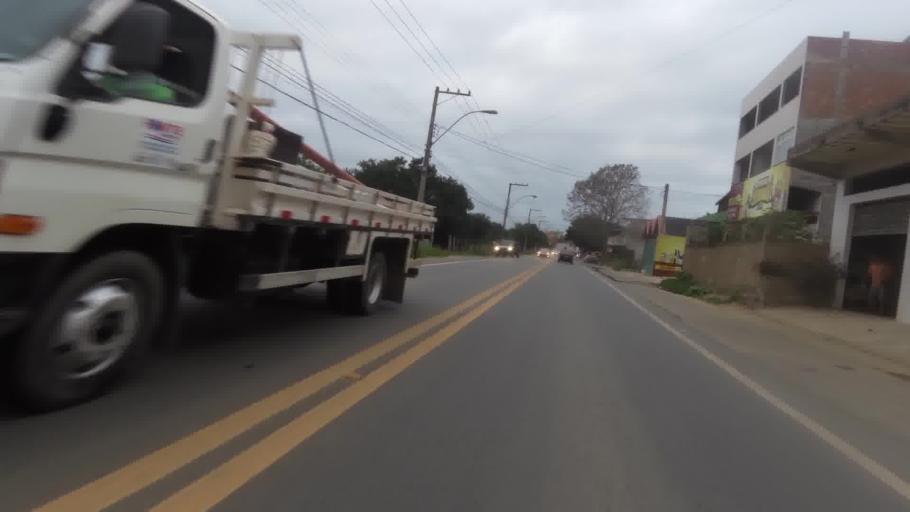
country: BR
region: Espirito Santo
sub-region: Piuma
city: Piuma
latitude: -20.8342
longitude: -40.7137
